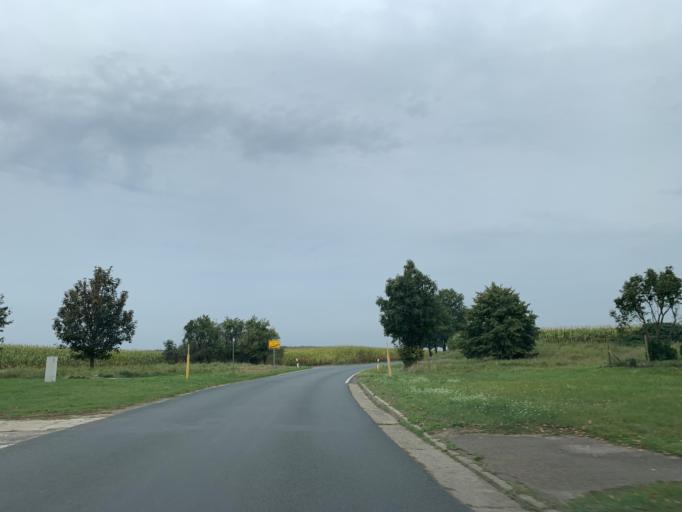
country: DE
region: Mecklenburg-Vorpommern
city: Woldegk
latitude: 53.3274
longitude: 13.5708
